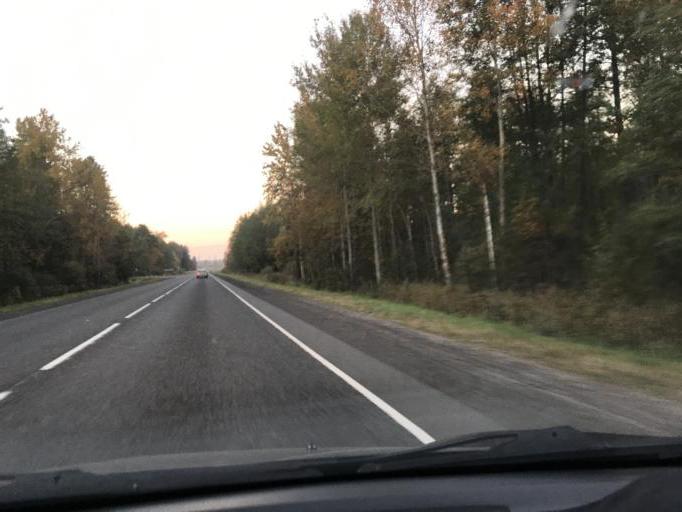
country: BY
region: Mogilev
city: Babruysk
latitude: 53.1675
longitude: 29.0450
